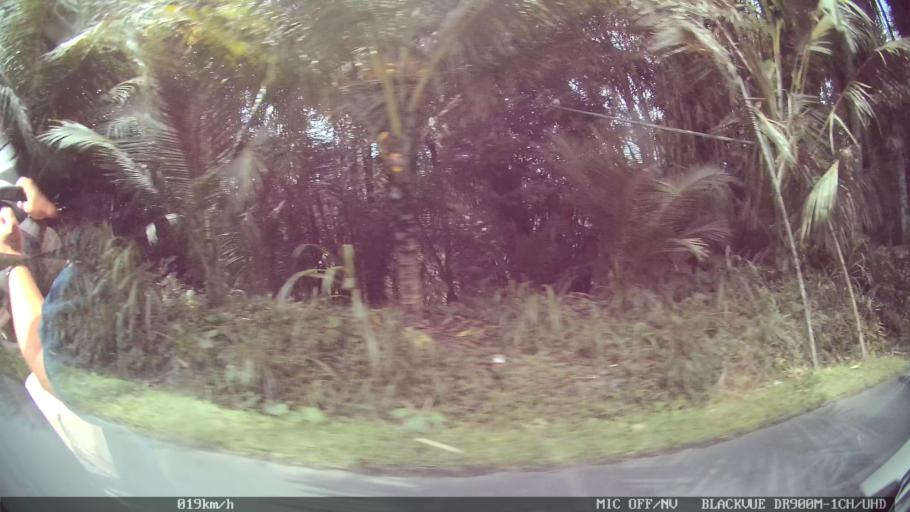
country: ID
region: Bali
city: Banjar Geriana Kangin
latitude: -8.4081
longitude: 115.4393
